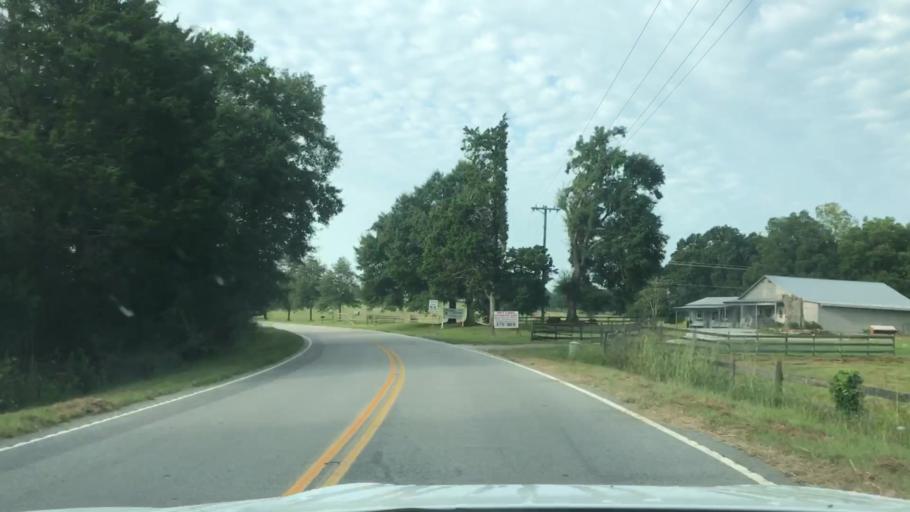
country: US
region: South Carolina
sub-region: Spartanburg County
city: Roebuck
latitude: 34.8183
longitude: -81.9267
